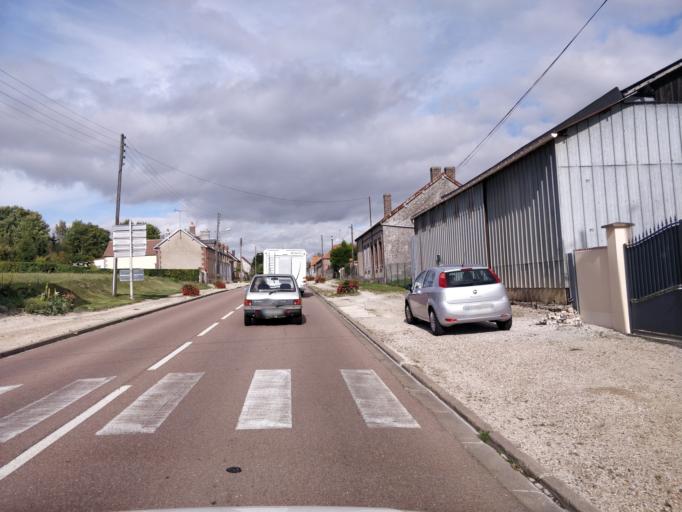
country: FR
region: Champagne-Ardenne
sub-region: Departement de l'Aube
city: Aix-en-Othe
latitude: 48.2540
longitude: 3.7229
